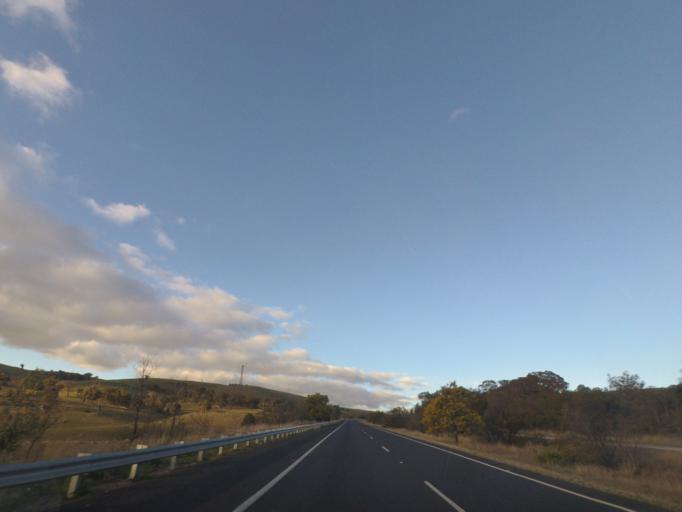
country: AU
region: New South Wales
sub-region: Yass Valley
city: Yass
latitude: -34.7785
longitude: 148.7181
